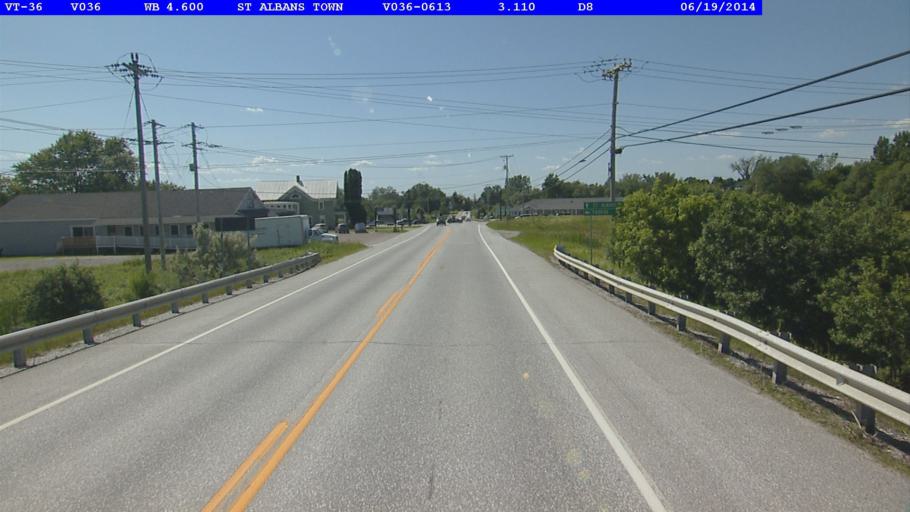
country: US
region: Vermont
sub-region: Franklin County
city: Saint Albans
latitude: 44.8044
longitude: -73.0670
